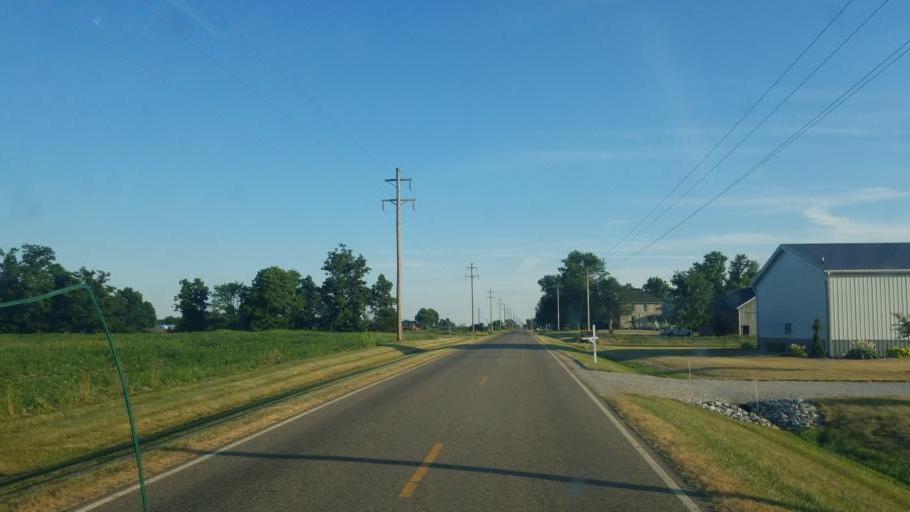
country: US
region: Ohio
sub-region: Defiance County
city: Hicksville
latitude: 41.3597
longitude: -84.7671
